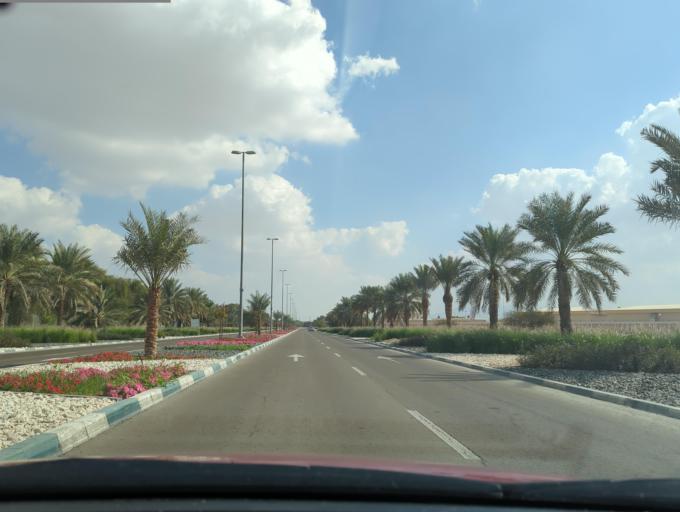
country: AE
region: Abu Dhabi
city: Al Ain
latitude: 24.1839
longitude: 55.6405
